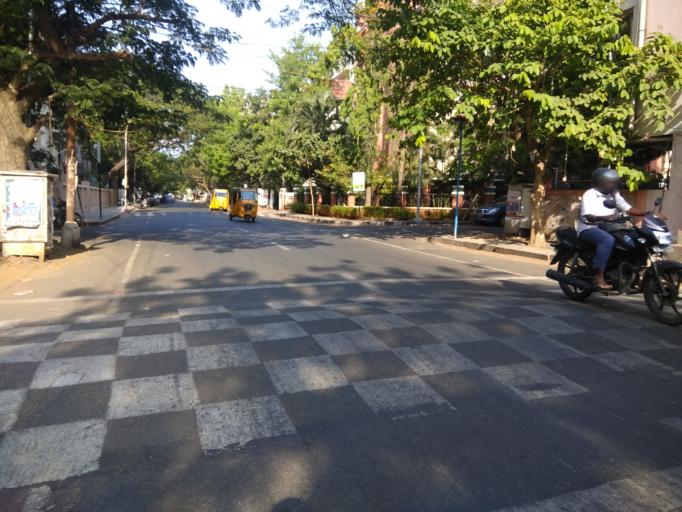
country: IN
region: Tamil Nadu
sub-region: Chennai
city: Gandhi Nagar
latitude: 13.0097
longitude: 80.2501
